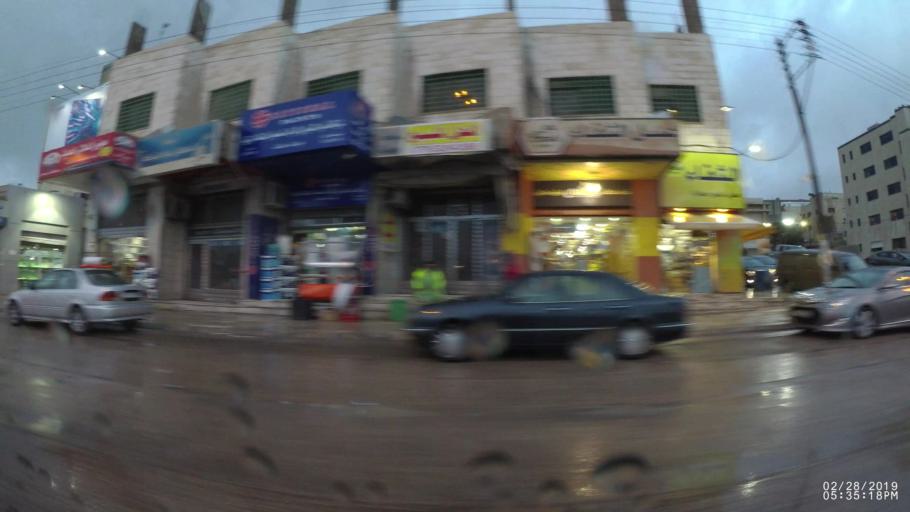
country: JO
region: Amman
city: Al Jubayhah
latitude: 31.9872
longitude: 35.9002
